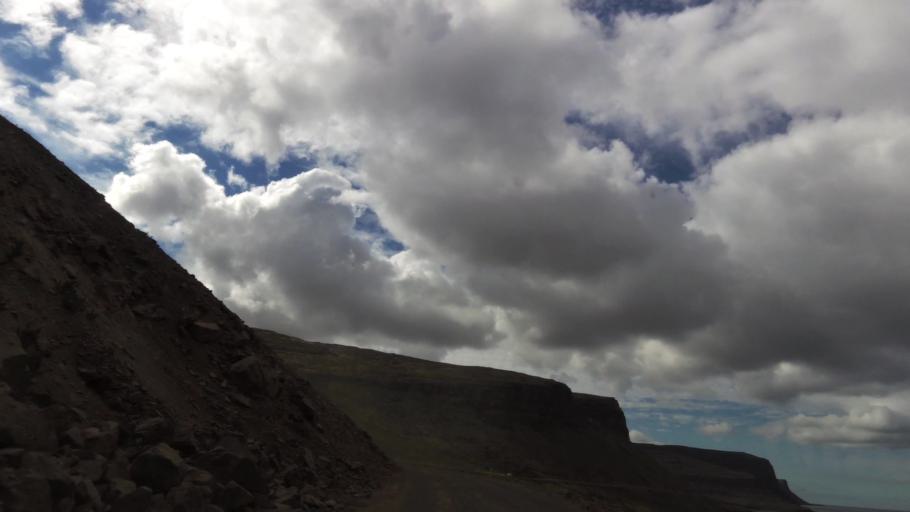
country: IS
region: West
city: Olafsvik
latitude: 65.5614
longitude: -24.0249
